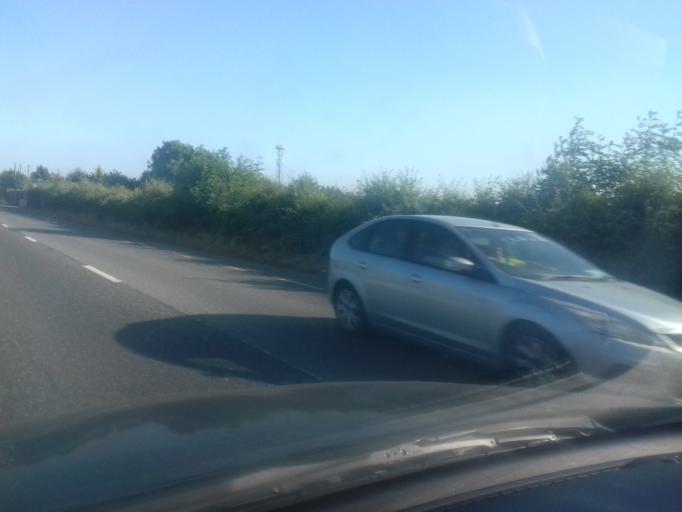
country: IE
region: Leinster
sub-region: Fingal County
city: Blanchardstown
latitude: 53.4507
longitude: -6.3447
